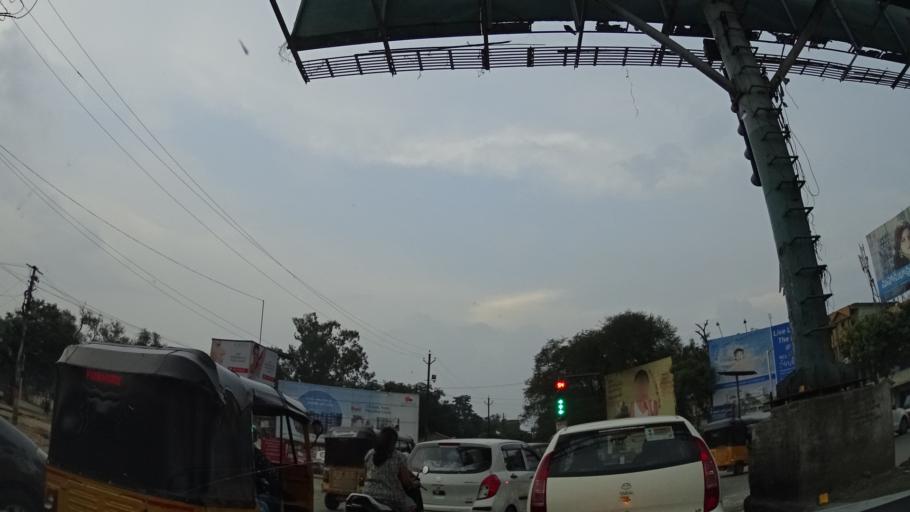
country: IN
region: Telangana
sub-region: Hyderabad
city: Malkajgiri
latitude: 17.4569
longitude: 78.4848
